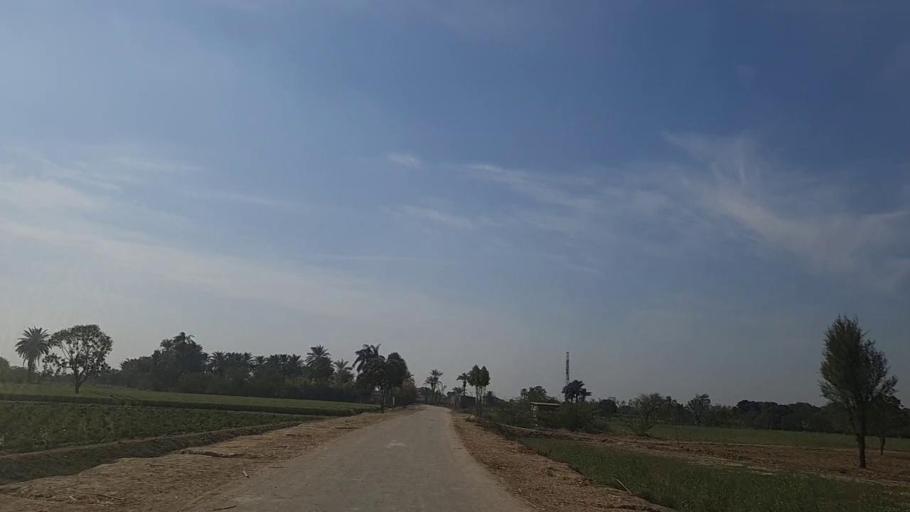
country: PK
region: Sindh
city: Mirpur Khas
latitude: 25.4699
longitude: 68.9643
